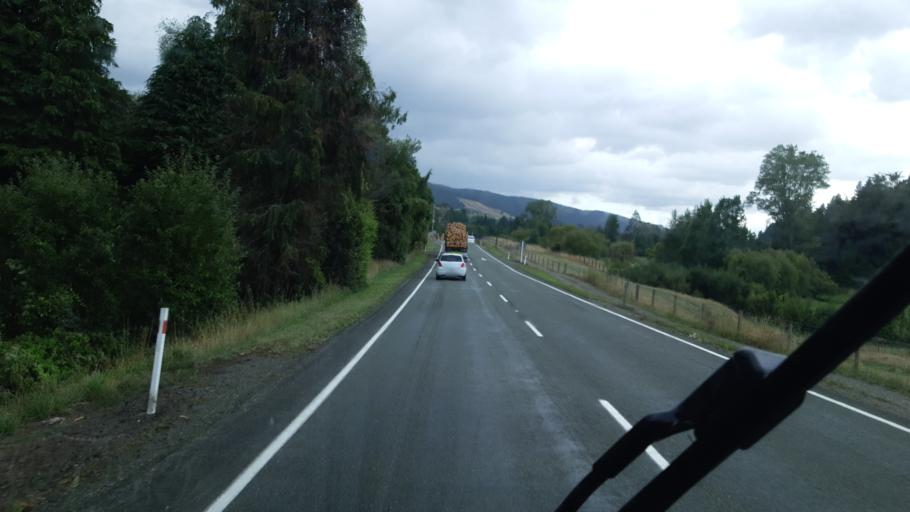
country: NZ
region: Tasman
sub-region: Tasman District
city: Wakefield
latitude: -41.4613
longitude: 172.9516
